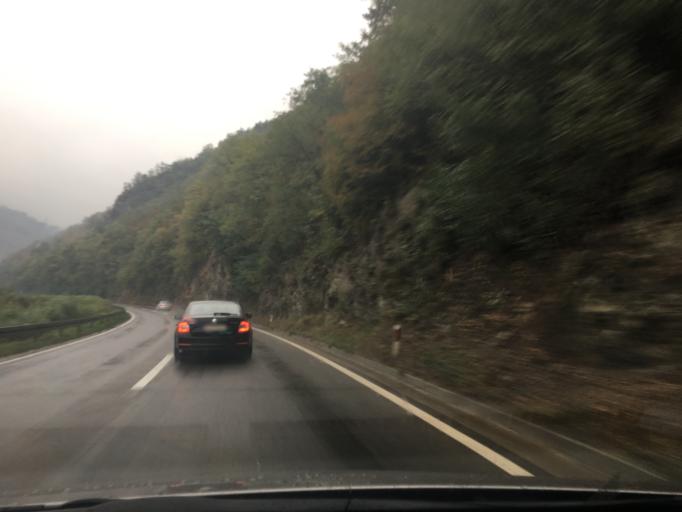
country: RS
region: Central Serbia
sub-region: Pcinjski Okrug
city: Vladicin Han
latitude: 42.7318
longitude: 22.0659
